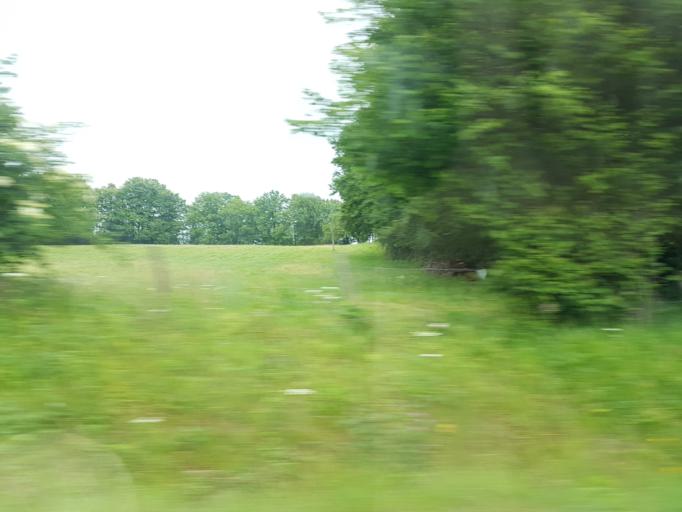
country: FR
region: Bourgogne
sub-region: Departement de la Nievre
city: Chateau-Chinon(Ville)
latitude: 47.0453
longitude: 4.0318
